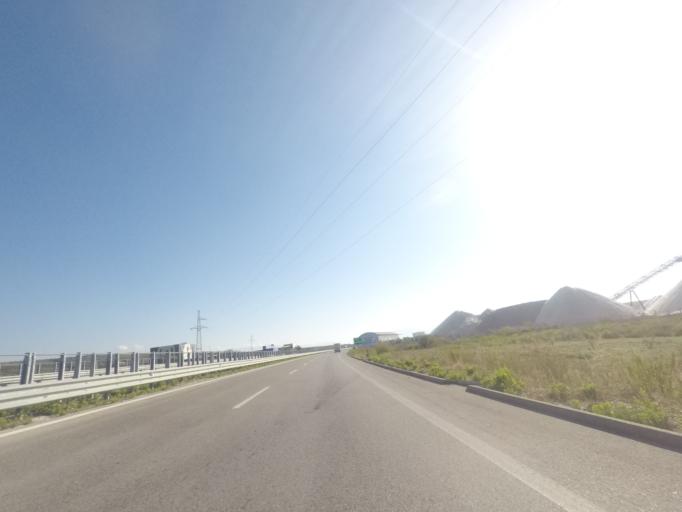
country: AL
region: Vlore
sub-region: Rrethi i Vlores
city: Novosele
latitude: 40.5668
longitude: 19.4689
